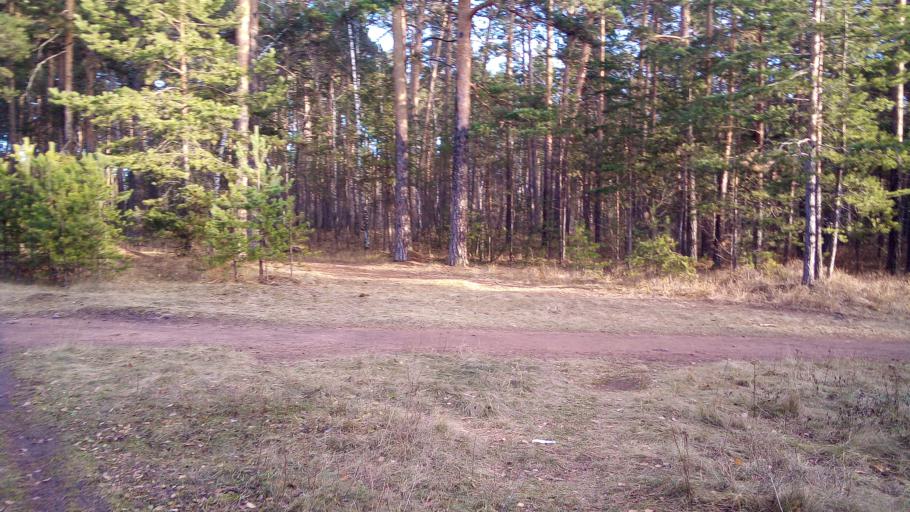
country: RU
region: Chelyabinsk
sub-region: Gorod Chelyabinsk
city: Chelyabinsk
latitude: 55.1549
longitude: 61.3508
